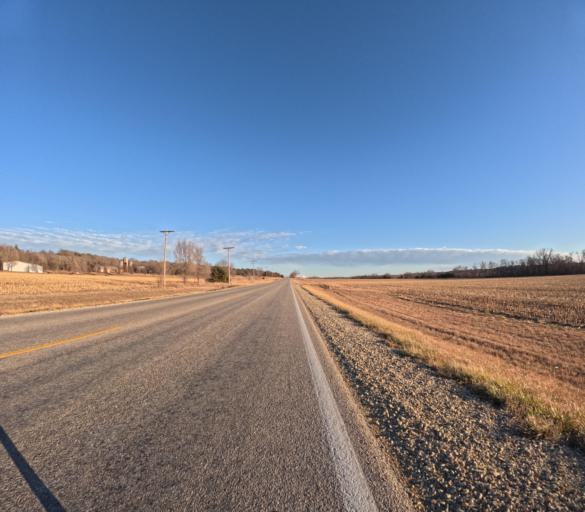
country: US
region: Kansas
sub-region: Riley County
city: Ogden
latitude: 39.2104
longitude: -96.6770
